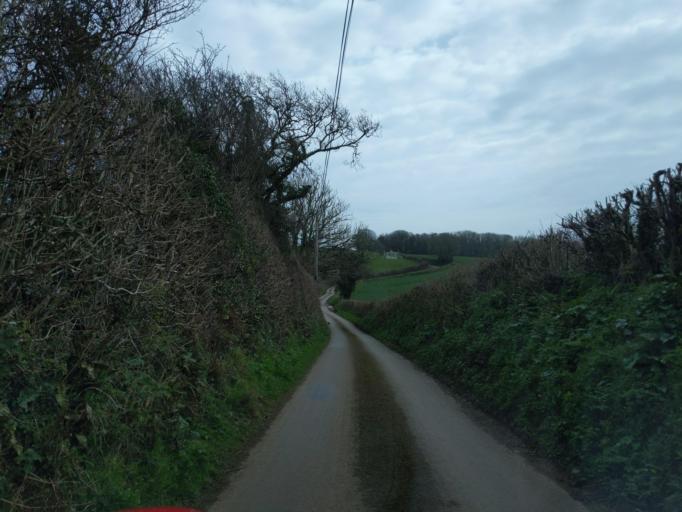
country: GB
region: England
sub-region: Devon
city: Yealmpton
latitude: 50.3621
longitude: -4.0040
